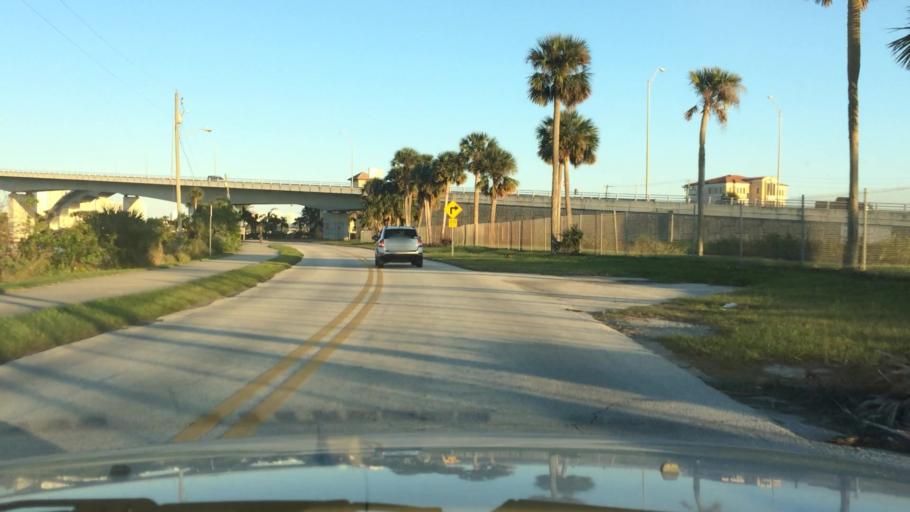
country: US
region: Florida
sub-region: Volusia County
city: Holly Hill
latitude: 29.2297
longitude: -81.0268
